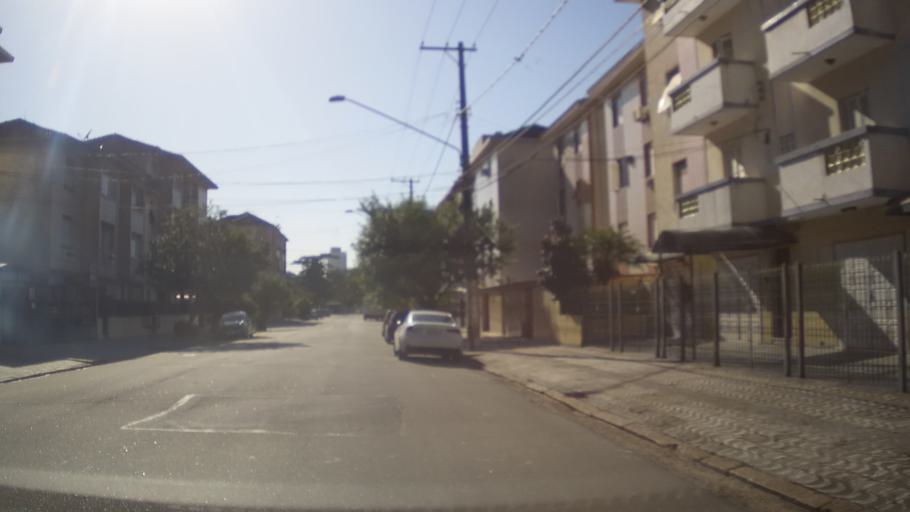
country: BR
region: Sao Paulo
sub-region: Santos
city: Santos
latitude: -23.9515
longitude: -46.3460
